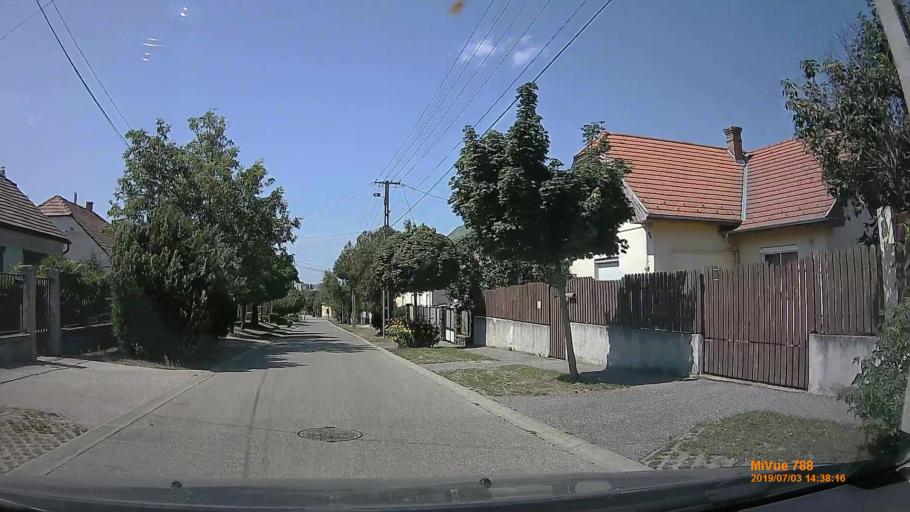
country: HU
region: Gyor-Moson-Sopron
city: Gyor
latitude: 47.6640
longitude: 17.6657
